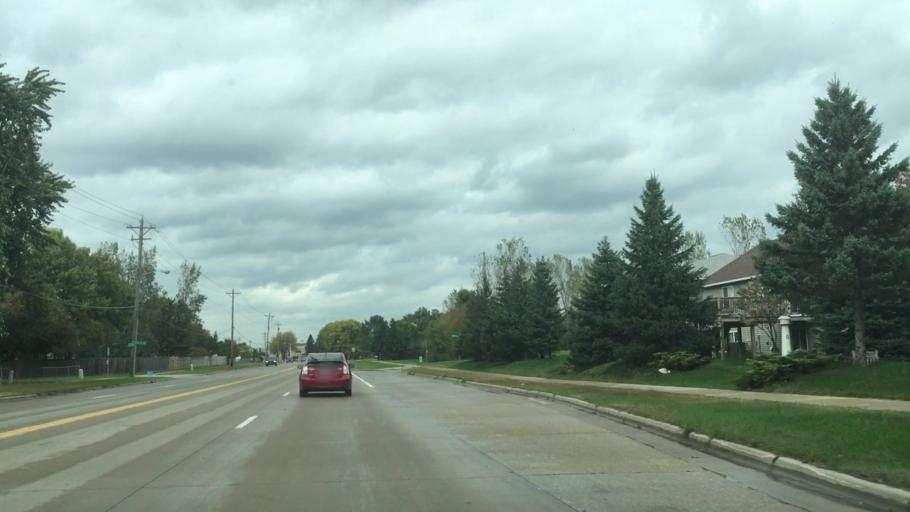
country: US
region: Minnesota
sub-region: Olmsted County
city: Rochester
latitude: 43.9965
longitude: -92.4441
